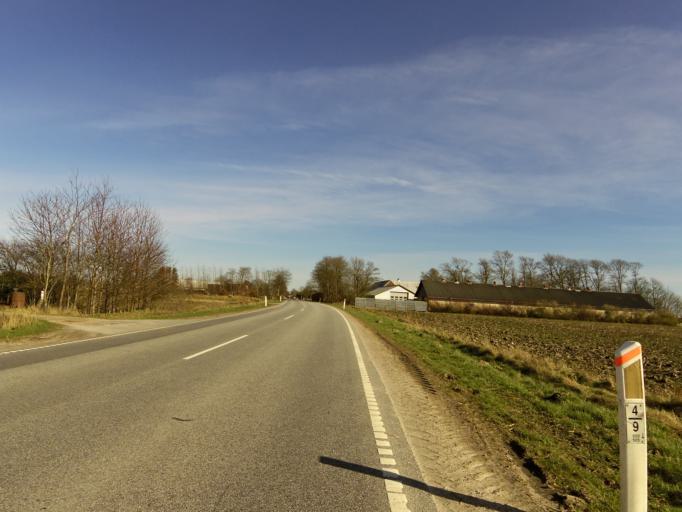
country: DK
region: South Denmark
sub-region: Vejen Kommune
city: Rodding
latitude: 55.3619
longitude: 9.1103
